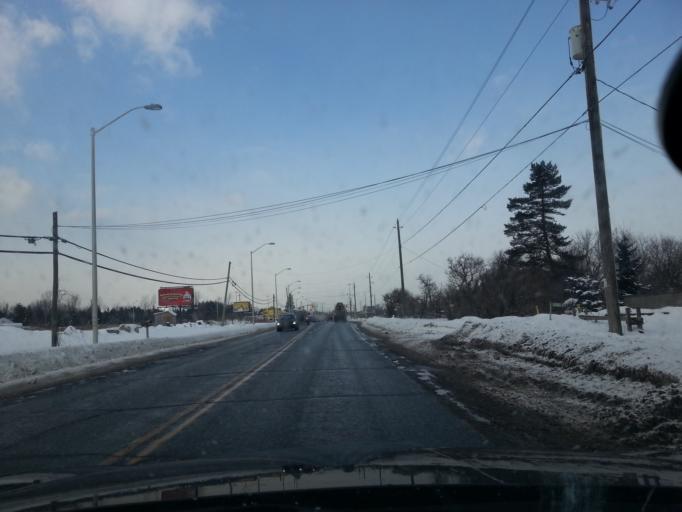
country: CA
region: Ontario
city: Bells Corners
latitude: 45.2762
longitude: -75.9508
